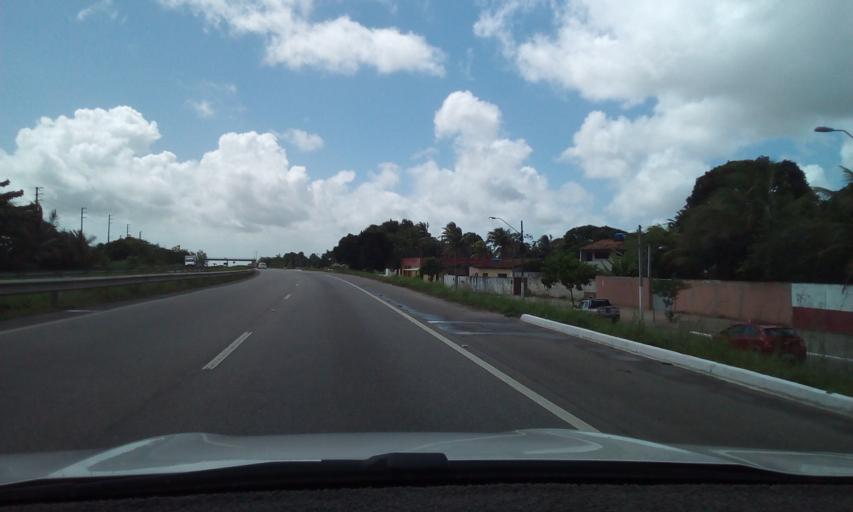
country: BR
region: Paraiba
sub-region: Bayeux
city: Bayeux
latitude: -7.1307
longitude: -34.9554
